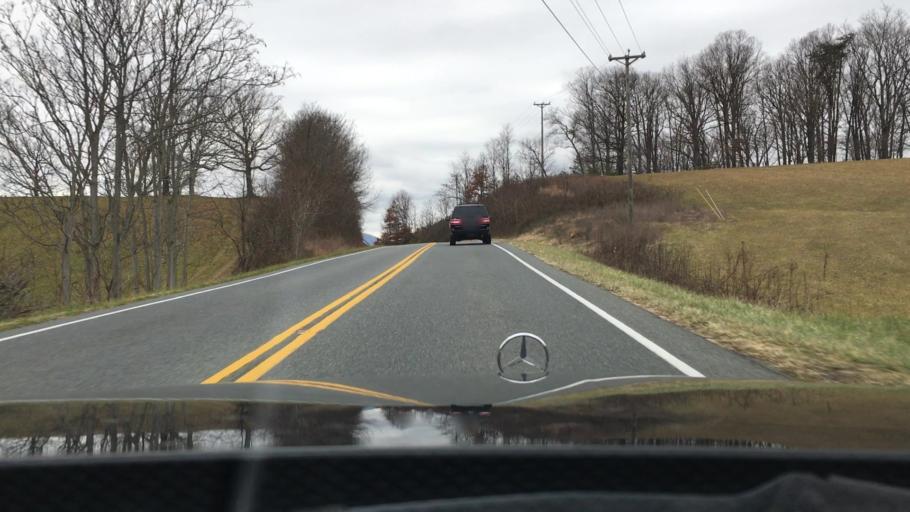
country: US
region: Virginia
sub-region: Franklin County
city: North Shore
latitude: 37.2479
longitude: -79.6875
